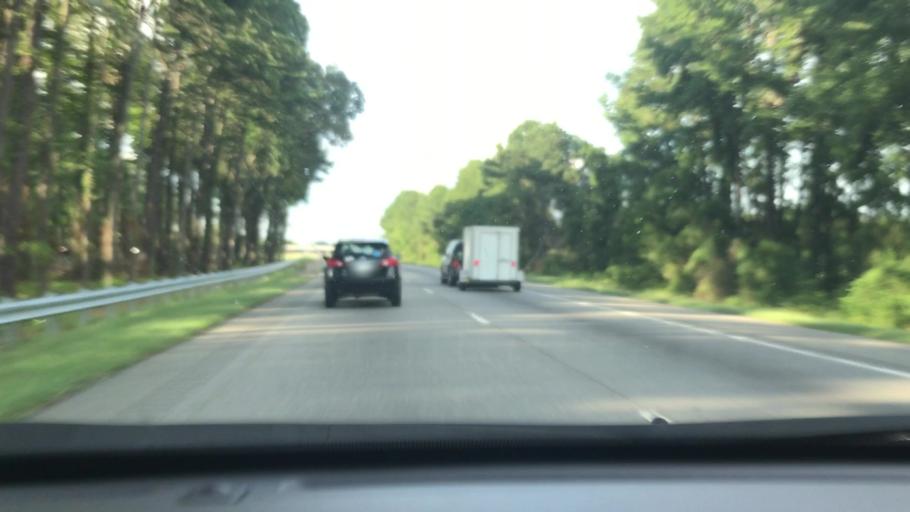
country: US
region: North Carolina
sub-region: Robeson County
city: Saint Pauls
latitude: 34.8414
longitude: -78.9727
